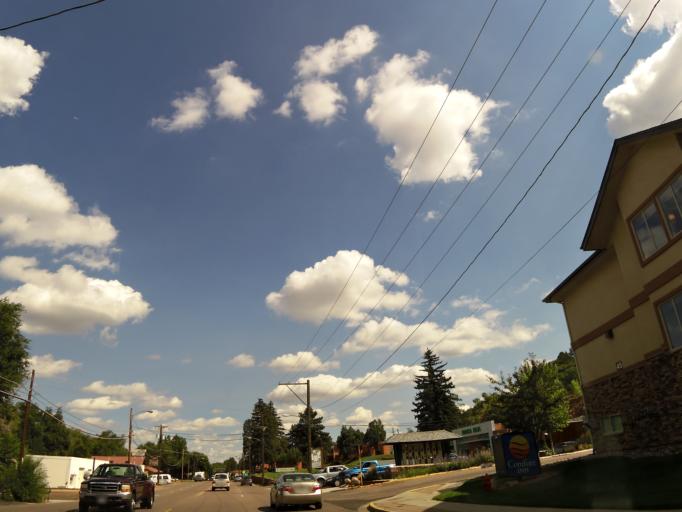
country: US
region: Colorado
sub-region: El Paso County
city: Manitou Springs
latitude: 38.8574
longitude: -104.8907
